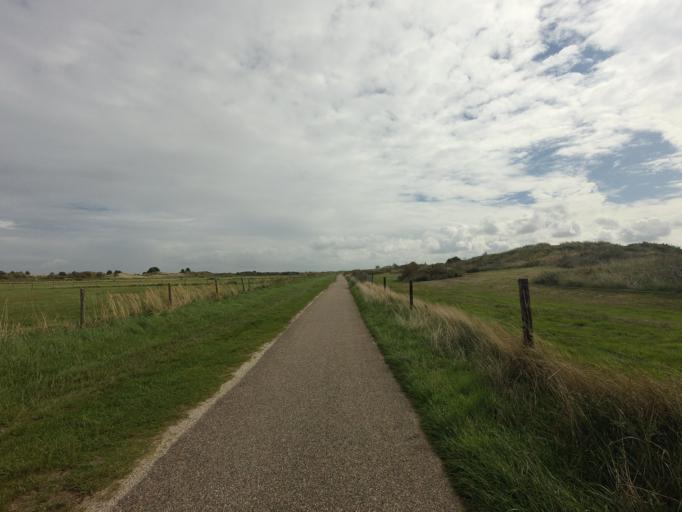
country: NL
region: Friesland
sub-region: Gemeente Ameland
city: Nes
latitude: 53.4555
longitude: 5.8162
